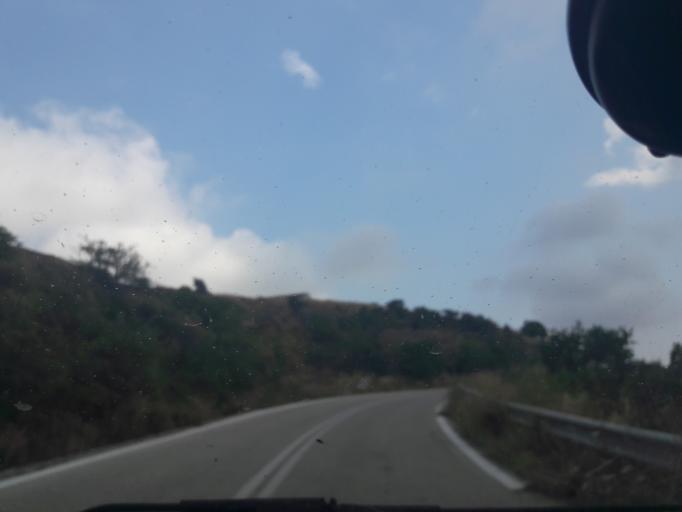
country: GR
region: North Aegean
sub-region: Nomos Lesvou
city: Myrina
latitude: 39.9517
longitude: 25.1660
